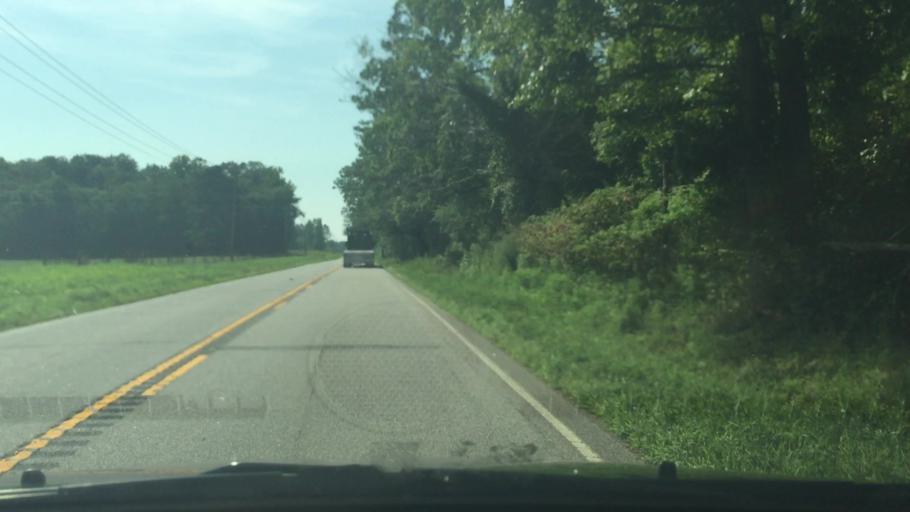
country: US
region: Virginia
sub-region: Sussex County
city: Sussex
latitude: 36.9965
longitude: -77.2607
